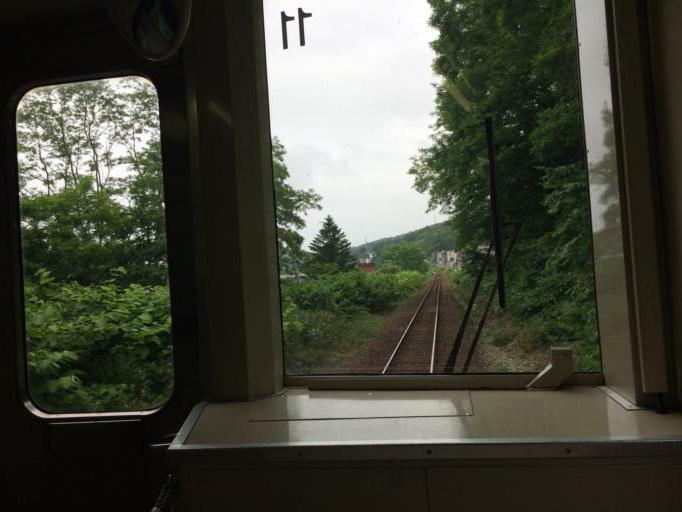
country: JP
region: Hokkaido
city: Otaru
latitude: 43.2100
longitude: 140.9651
